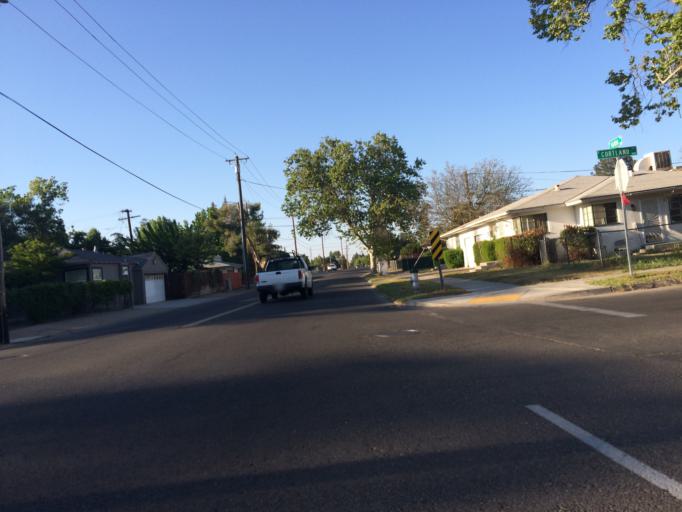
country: US
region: California
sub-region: Fresno County
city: Fresno
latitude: 36.7820
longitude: -119.7996
